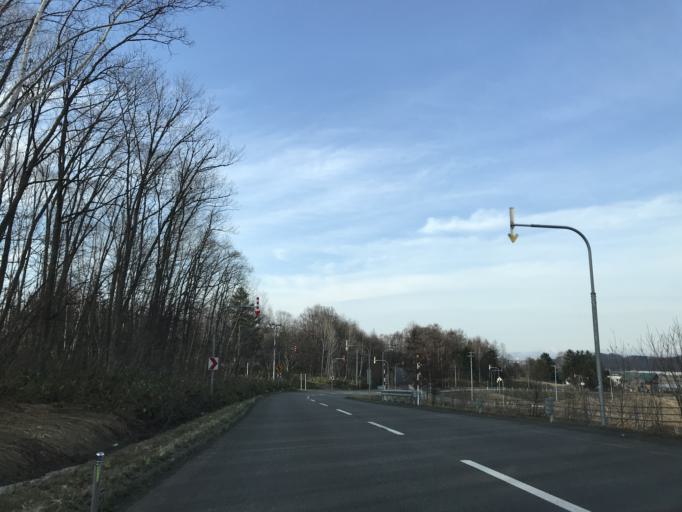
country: JP
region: Hokkaido
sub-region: Asahikawa-shi
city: Asahikawa
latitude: 43.6958
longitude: 142.3333
